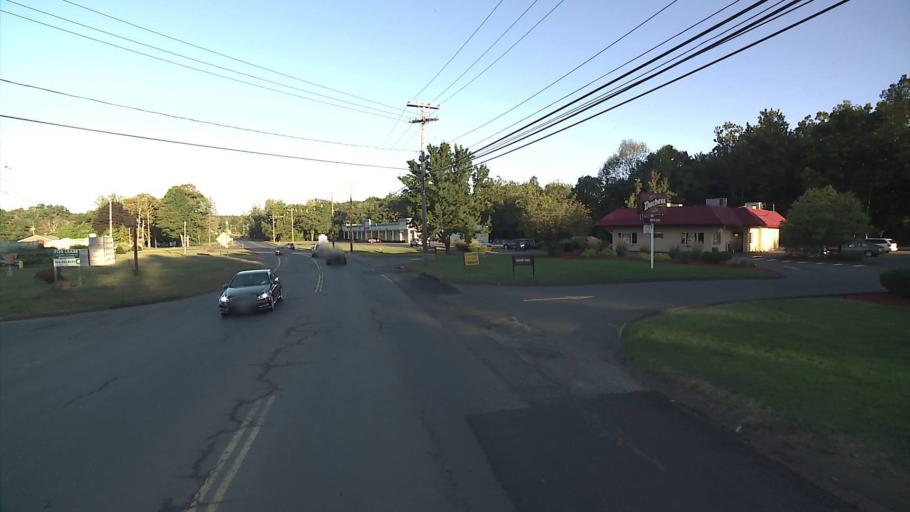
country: US
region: Connecticut
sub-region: New Haven County
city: Wallingford
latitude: 41.4900
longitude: -72.8132
